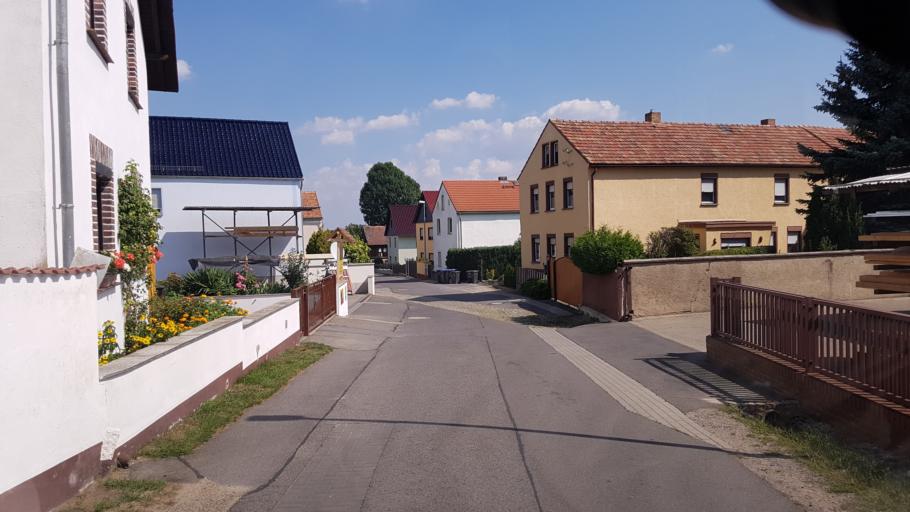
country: DE
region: Brandenburg
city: Hirschfeld
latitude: 51.3838
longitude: 13.6159
